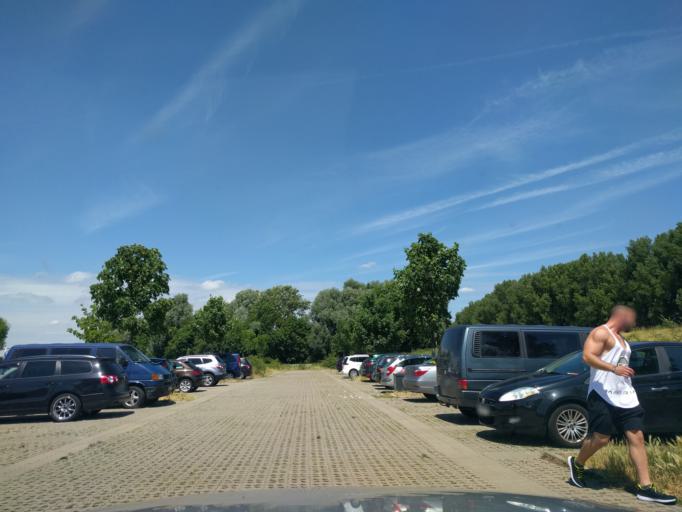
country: DE
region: North Rhine-Westphalia
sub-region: Regierungsbezirk Dusseldorf
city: Meerbusch
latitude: 51.2689
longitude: 6.6983
